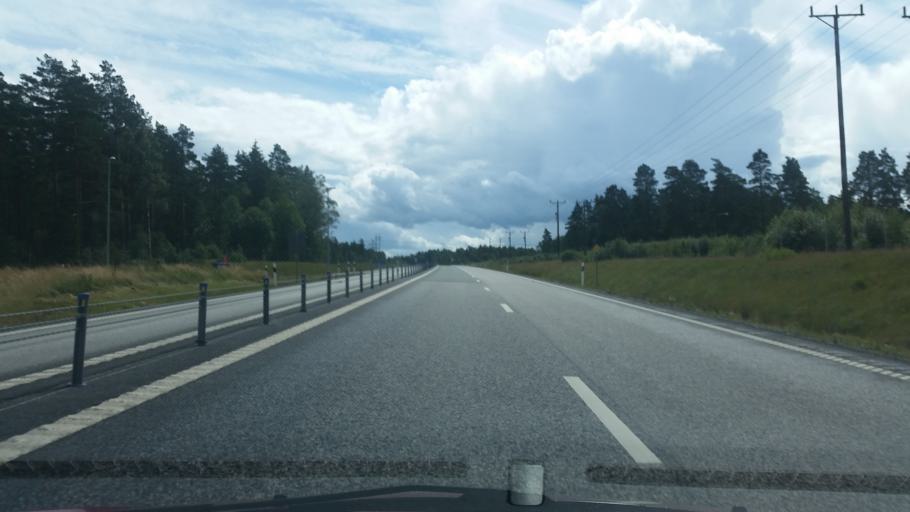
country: SE
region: Joenkoeping
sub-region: Gislaveds Kommun
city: Gislaved
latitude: 57.2996
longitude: 13.5843
